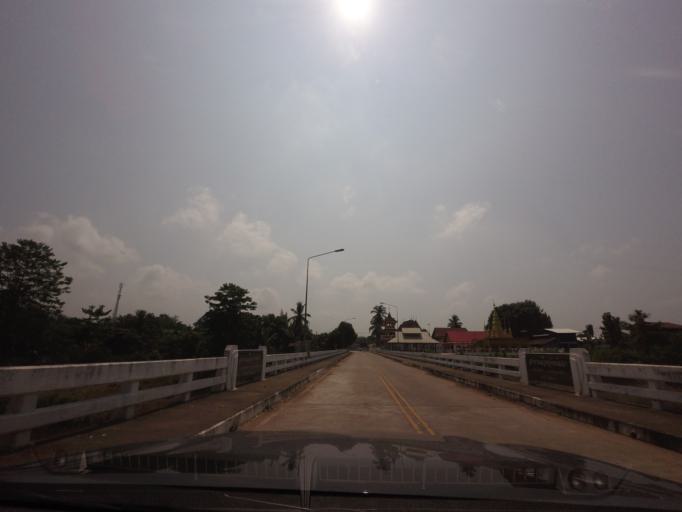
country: TH
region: Nan
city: Nan
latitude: 18.8598
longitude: 100.8170
